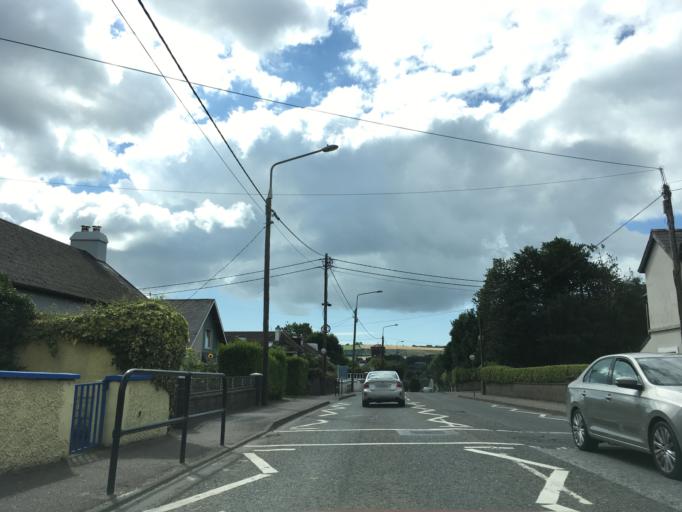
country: IE
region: Munster
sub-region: County Cork
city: Carrigaline
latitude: 51.8186
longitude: -8.3916
